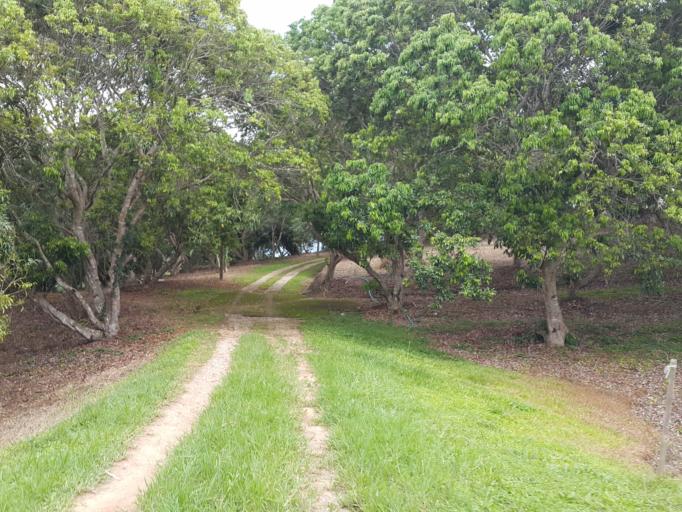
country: TH
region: Chiang Mai
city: San Sai
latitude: 18.9331
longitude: 98.9153
